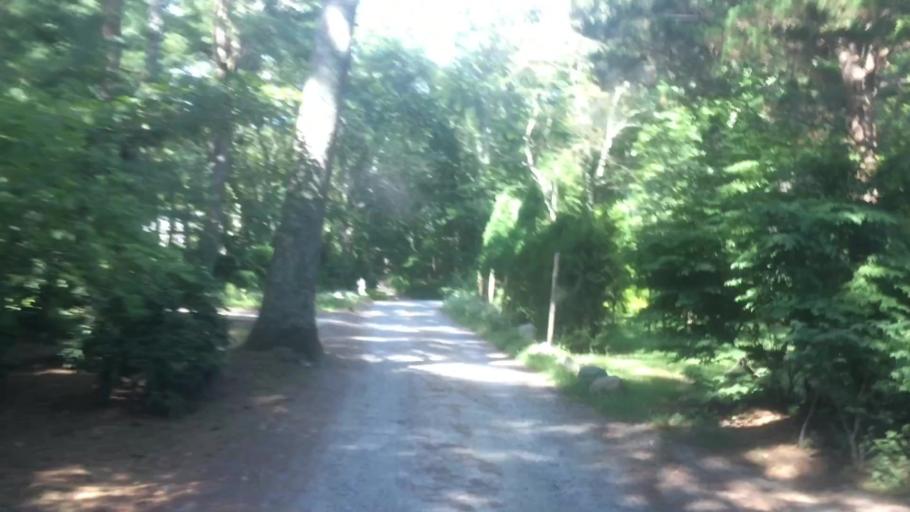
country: US
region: Rhode Island
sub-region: Newport County
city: Jamestown
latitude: 41.5042
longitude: -71.4209
